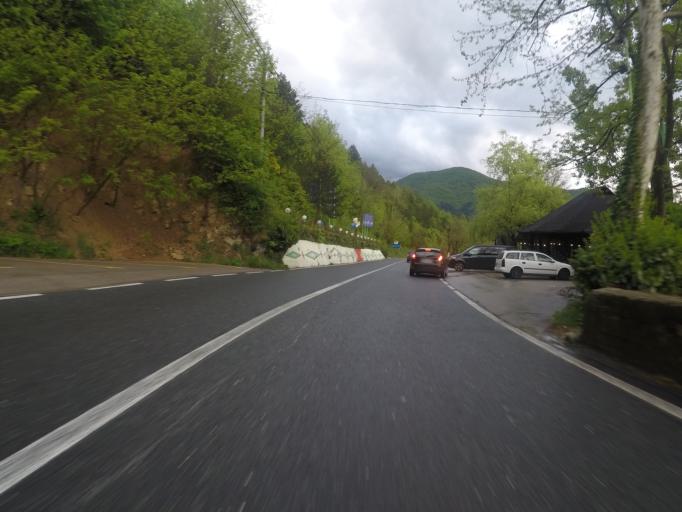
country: BA
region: Federation of Bosnia and Herzegovina
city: Jablanica
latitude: 43.6506
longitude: 17.7537
